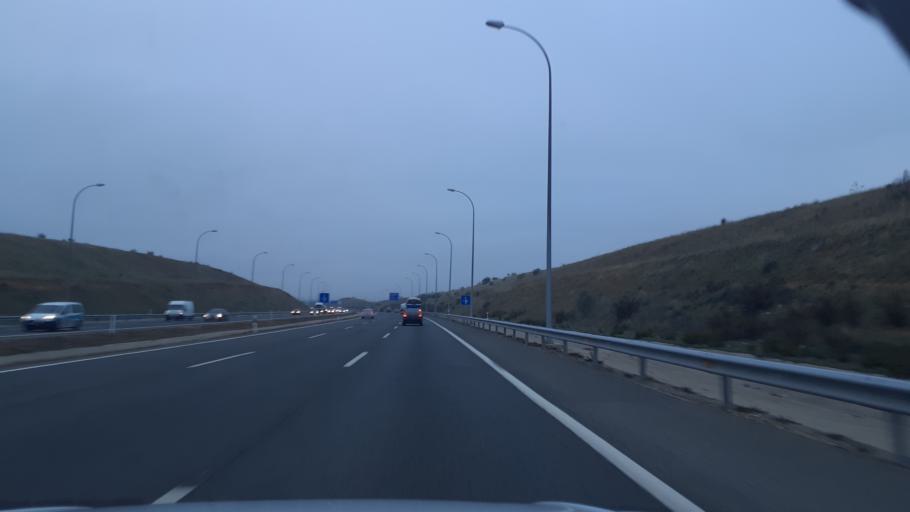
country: ES
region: Madrid
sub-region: Provincia de Madrid
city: Paracuellos de Jarama
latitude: 40.4937
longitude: -3.4959
